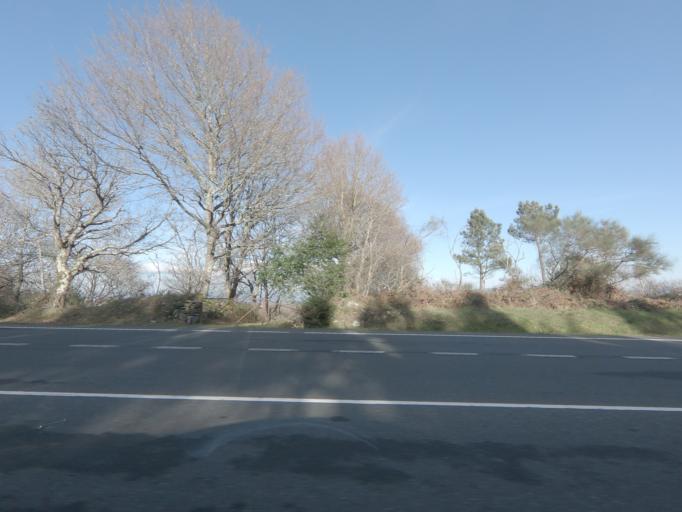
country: ES
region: Galicia
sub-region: Provincia de Pontevedra
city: Silleda
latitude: 42.7057
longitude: -8.3447
